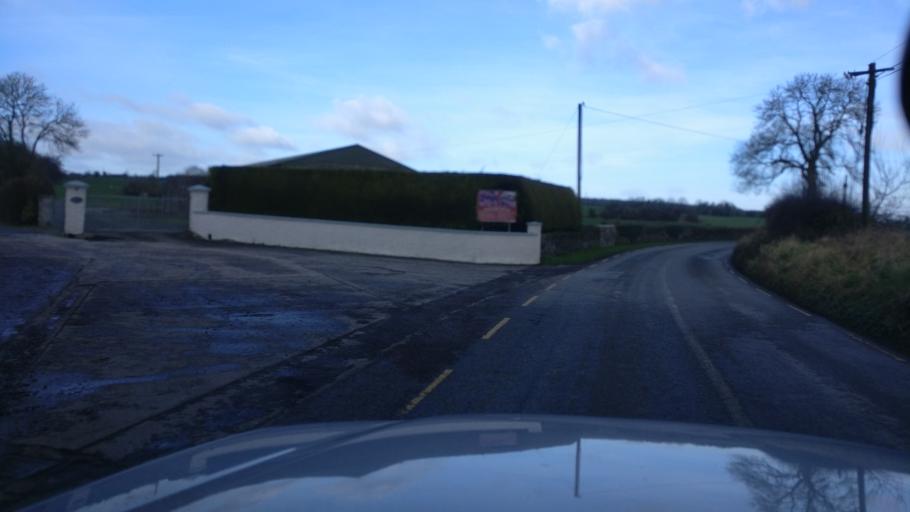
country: IE
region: Leinster
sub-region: Kilkenny
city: Castlecomer
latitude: 52.8260
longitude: -7.2080
